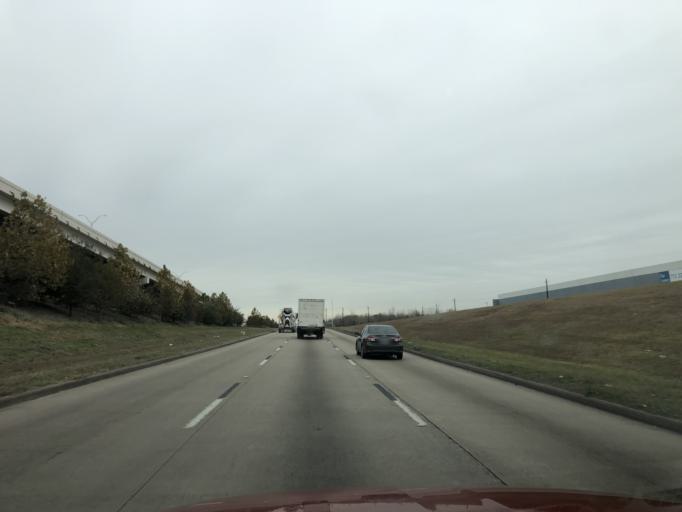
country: US
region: Texas
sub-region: Fort Bend County
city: Missouri City
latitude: 29.6272
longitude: -95.5183
